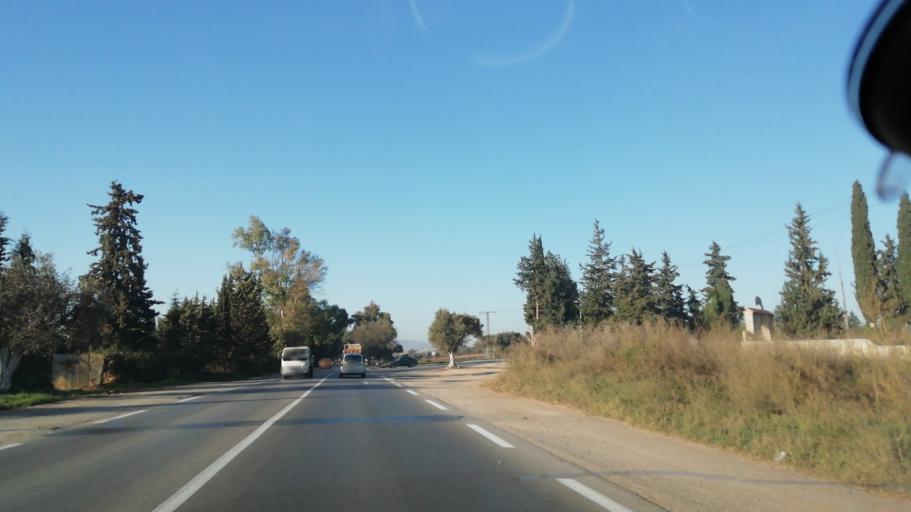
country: DZ
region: Tlemcen
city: Remchi
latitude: 35.0713
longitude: -1.4612
